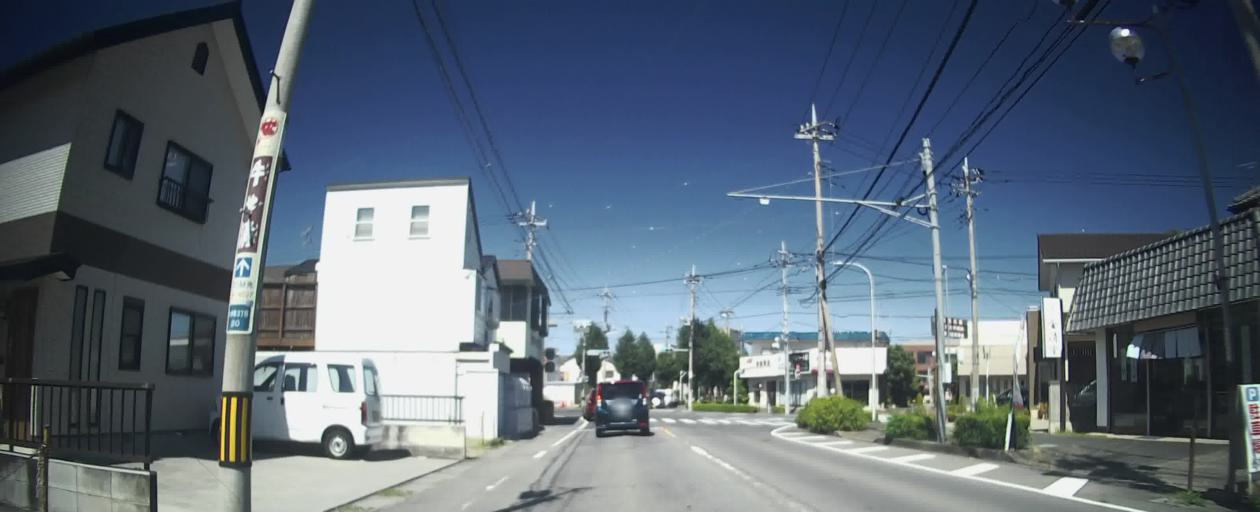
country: JP
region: Gunma
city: Maebashi-shi
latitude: 36.4060
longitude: 139.0537
